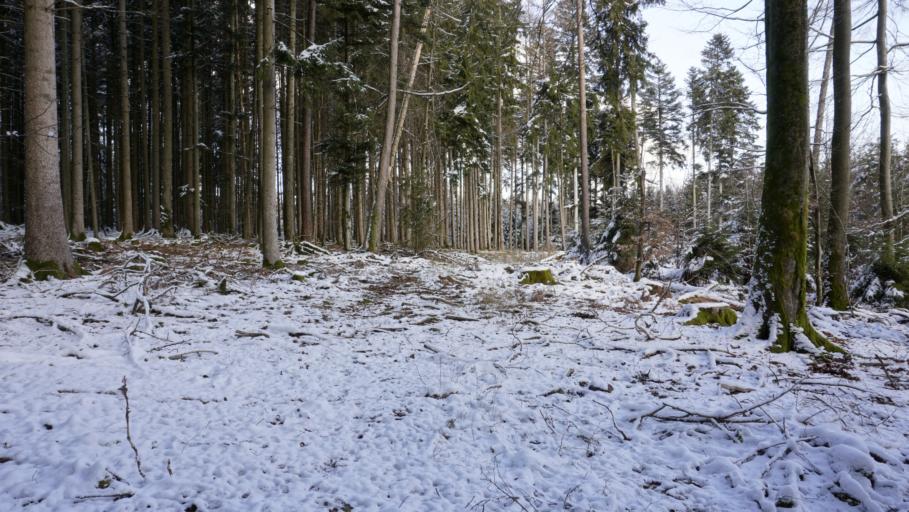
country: DE
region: Baden-Wuerttemberg
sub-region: Karlsruhe Region
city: Fahrenbach
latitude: 49.4352
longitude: 9.1191
